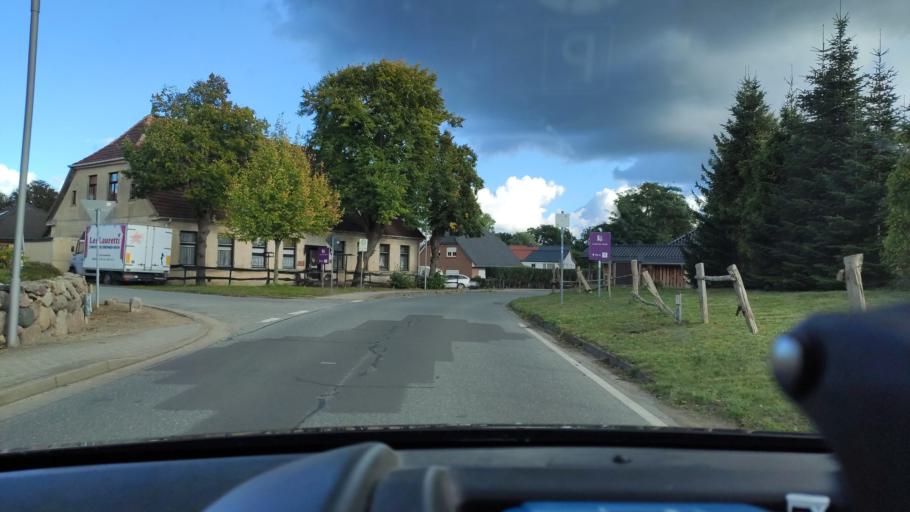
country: DE
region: Mecklenburg-Vorpommern
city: Butzow
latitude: 53.8226
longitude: 11.9354
